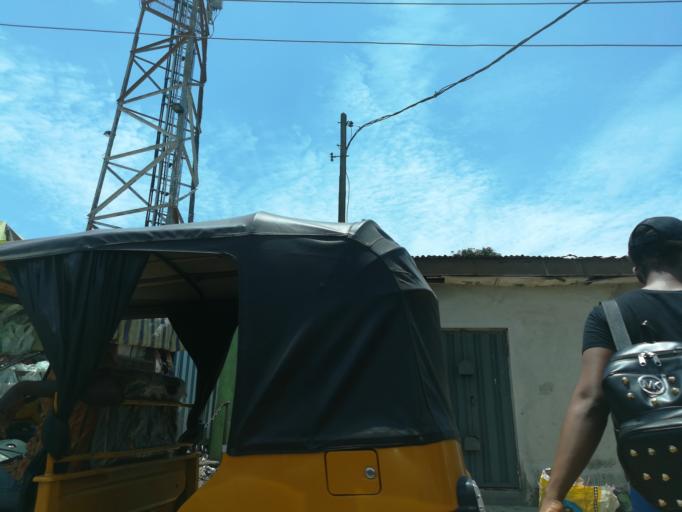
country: NG
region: Lagos
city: Ebute Ikorodu
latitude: 6.6018
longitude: 3.4922
